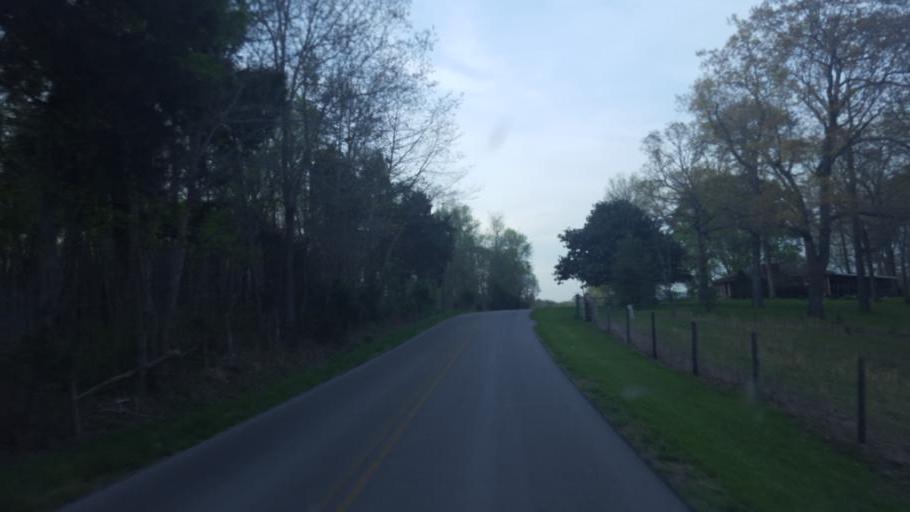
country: US
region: Kentucky
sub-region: Metcalfe County
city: Edmonton
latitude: 37.0694
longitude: -85.7076
